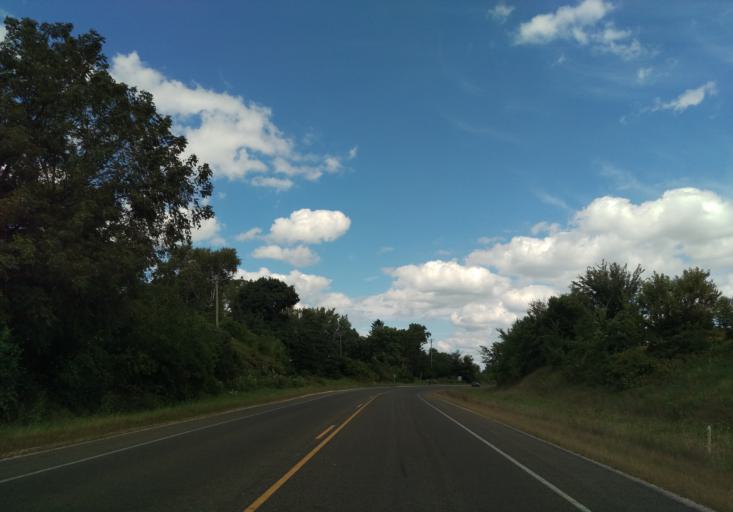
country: US
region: Wisconsin
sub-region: Dane County
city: Waunakee
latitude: 43.1428
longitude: -89.4422
